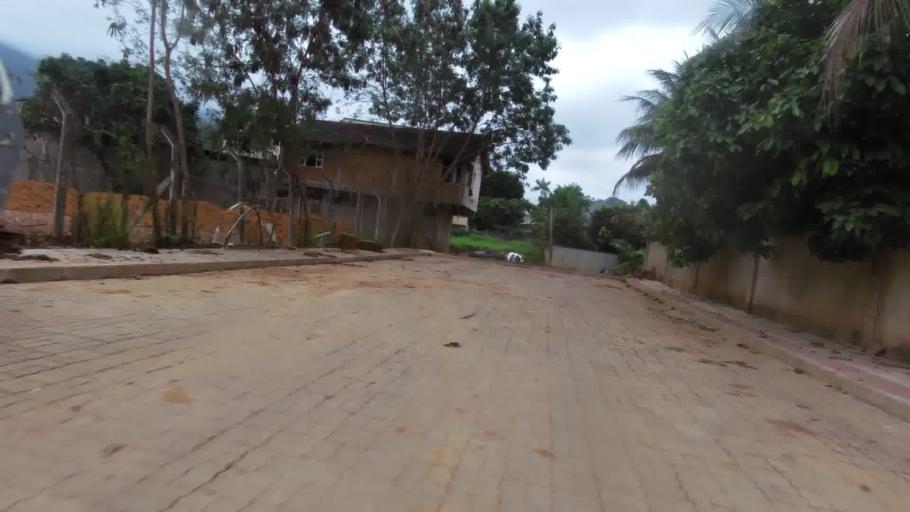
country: BR
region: Espirito Santo
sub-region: Alfredo Chaves
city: Alfredo Chaves
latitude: -20.6405
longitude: -40.7453
